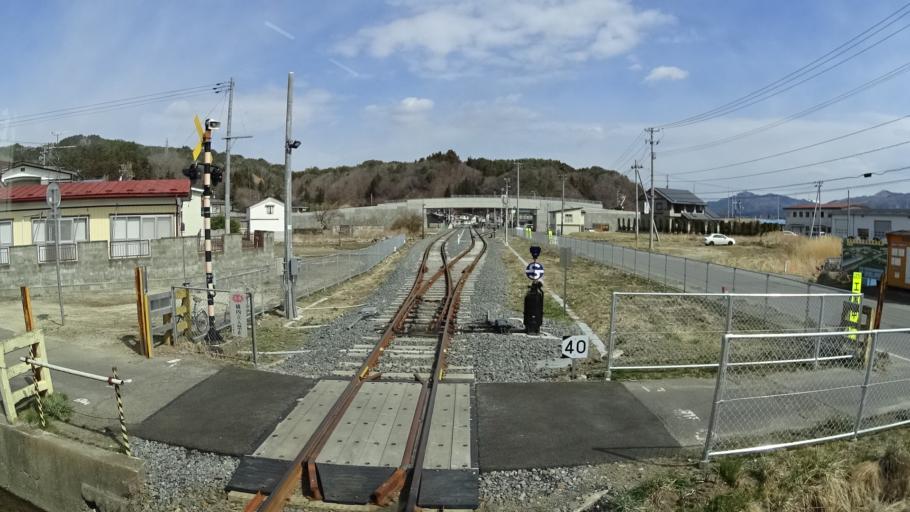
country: JP
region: Iwate
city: Miyako
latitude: 39.5799
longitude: 141.9369
